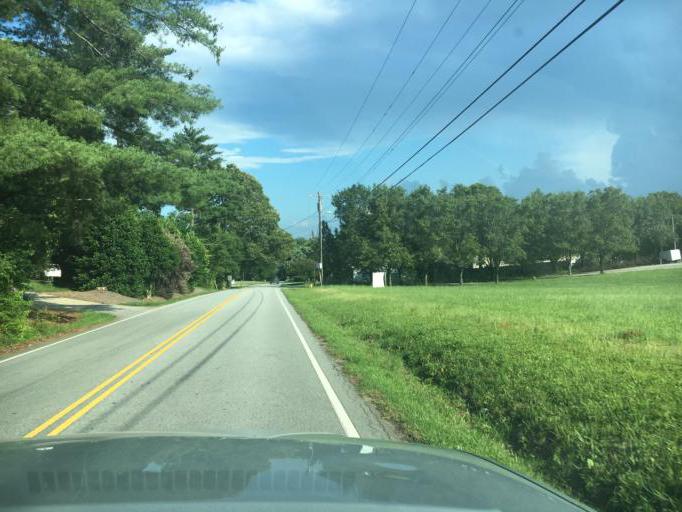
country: US
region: South Carolina
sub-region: Greenville County
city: Mauldin
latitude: 34.7774
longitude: -82.2724
